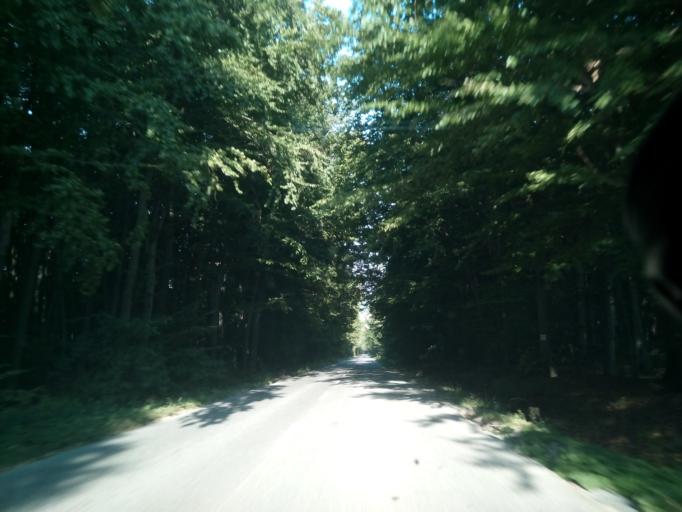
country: SK
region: Kosicky
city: Kosice
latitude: 48.7252
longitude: 21.1300
